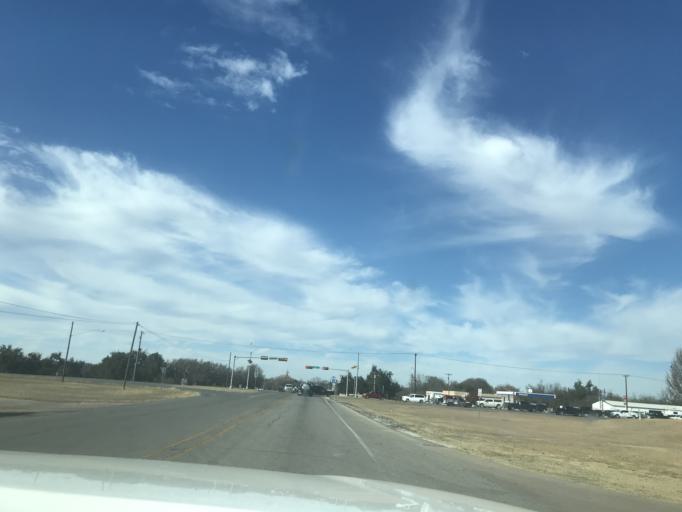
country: US
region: Texas
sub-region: Erath County
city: Stephenville
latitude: 32.2110
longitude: -98.1955
